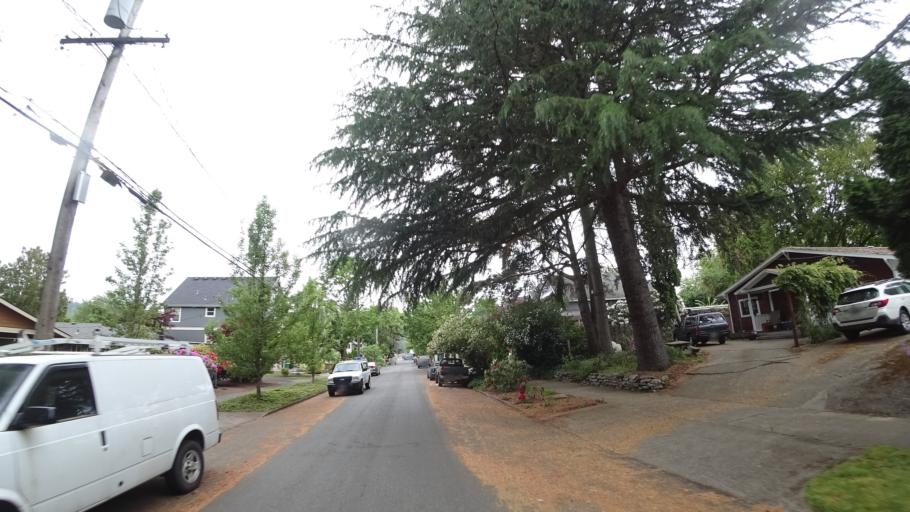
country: US
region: Oregon
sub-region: Clackamas County
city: Milwaukie
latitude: 45.4600
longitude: -122.6554
